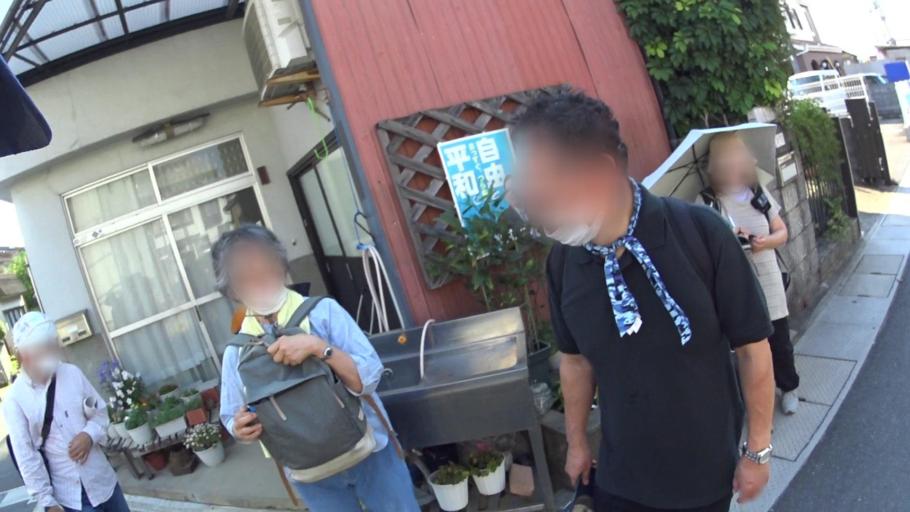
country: JP
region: Kyoto
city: Yawata
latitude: 34.8983
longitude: 135.7159
